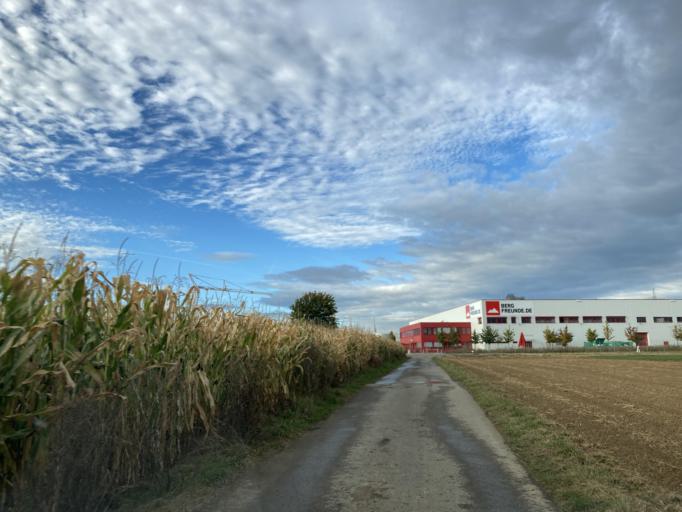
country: DE
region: Baden-Wuerttemberg
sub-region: Regierungsbezirk Stuttgart
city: Bondorf
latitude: 48.4961
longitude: 8.8235
